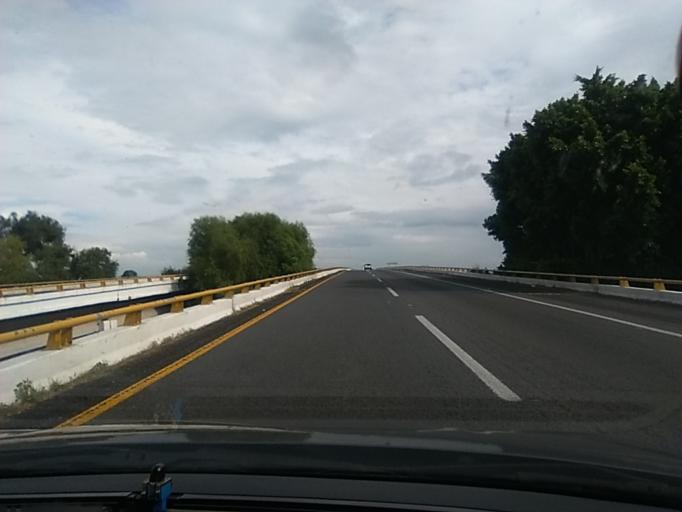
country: MX
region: Michoacan
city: Vistahermosa de Negrete
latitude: 20.3087
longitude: -102.4923
